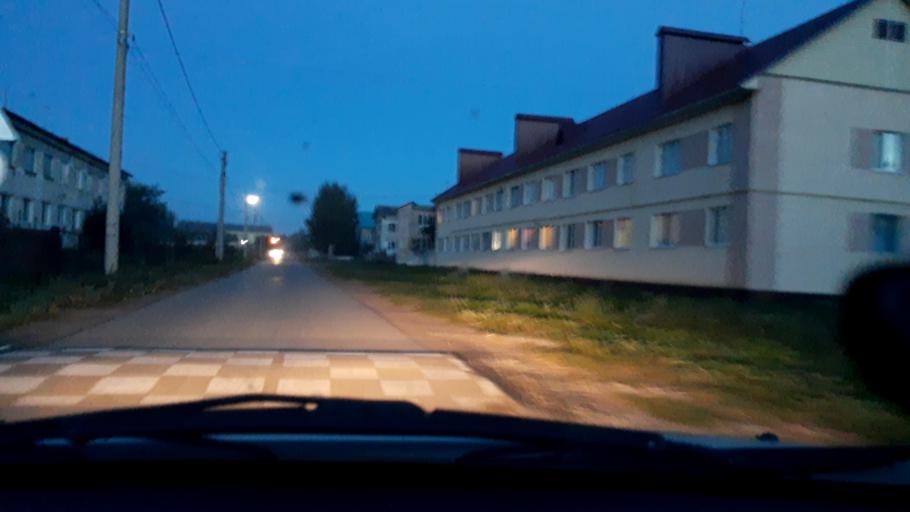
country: RU
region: Bashkortostan
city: Ulukulevo
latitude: 54.4235
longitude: 56.3363
